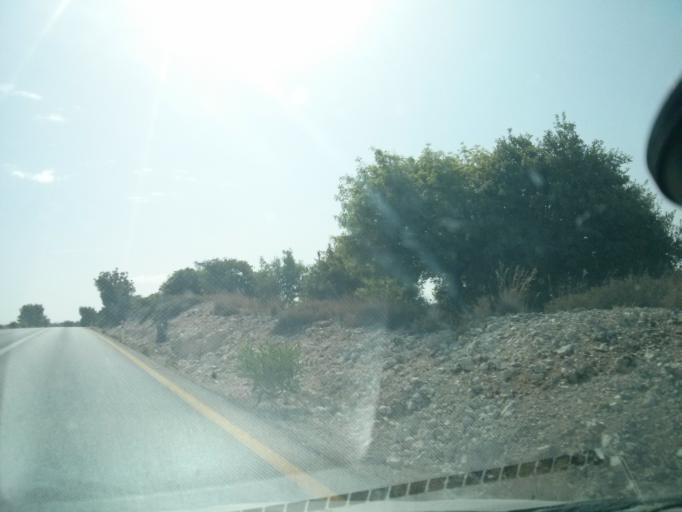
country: PS
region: West Bank
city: Surif
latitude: 31.6749
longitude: 35.0297
